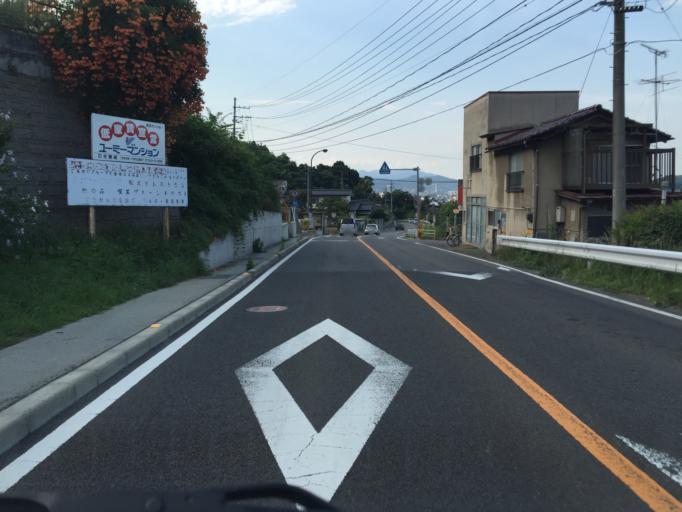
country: JP
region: Fukushima
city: Fukushima-shi
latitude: 37.7171
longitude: 140.4620
